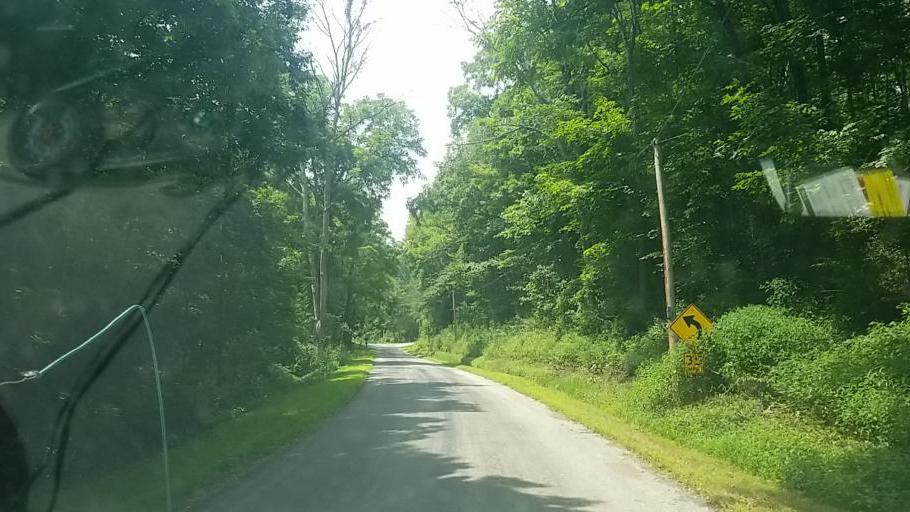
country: US
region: Ohio
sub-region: Muskingum County
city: Frazeysburg
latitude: 40.2192
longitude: -82.2486
